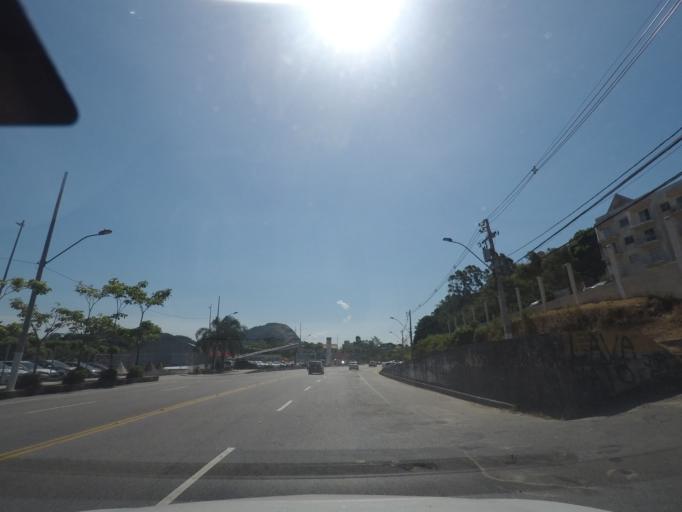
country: BR
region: Rio de Janeiro
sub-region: Niteroi
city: Niteroi
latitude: -22.9116
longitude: -43.0582
